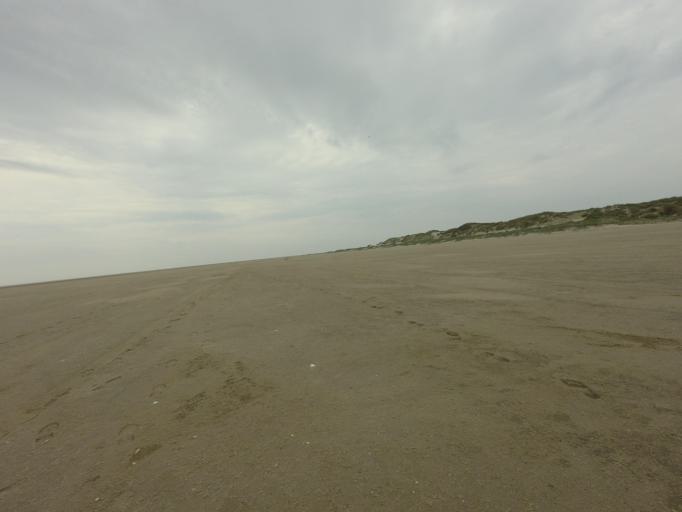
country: NL
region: North Holland
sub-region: Gemeente Den Helder
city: Den Helder
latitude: 52.9928
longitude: 4.7475
